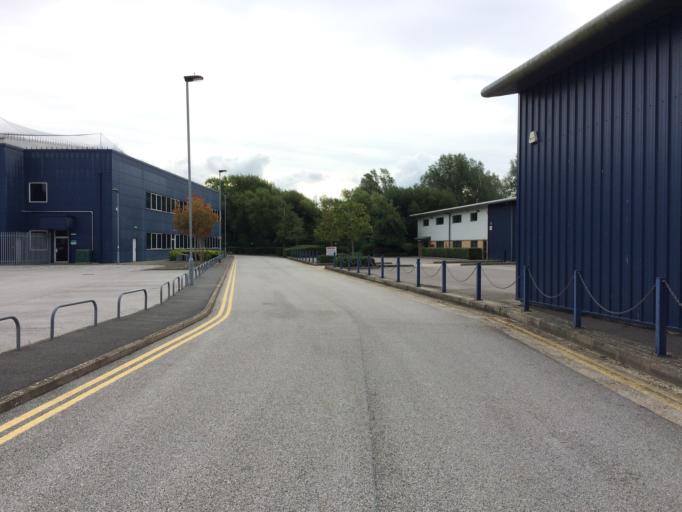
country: GB
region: England
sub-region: East Sussex
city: Hailsham
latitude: 50.8591
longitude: 0.2488
